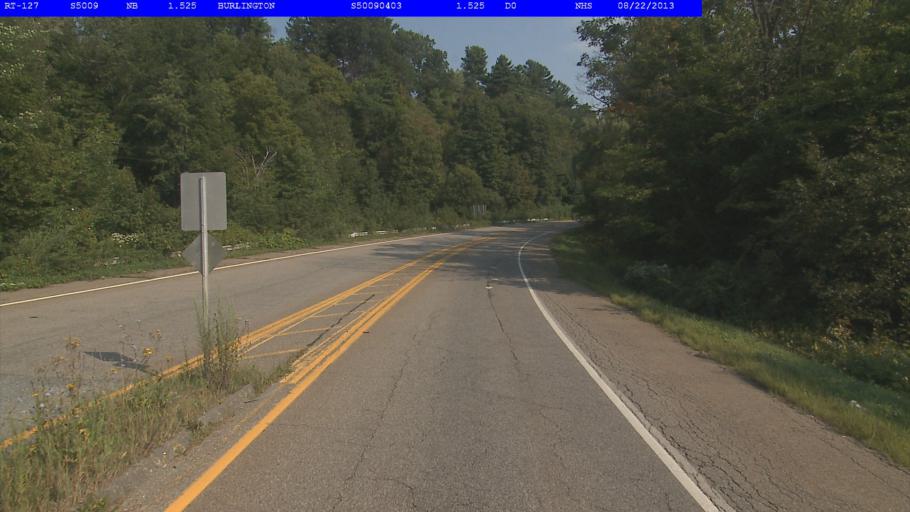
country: US
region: Vermont
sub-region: Chittenden County
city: Burlington
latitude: 44.5064
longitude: -73.2339
